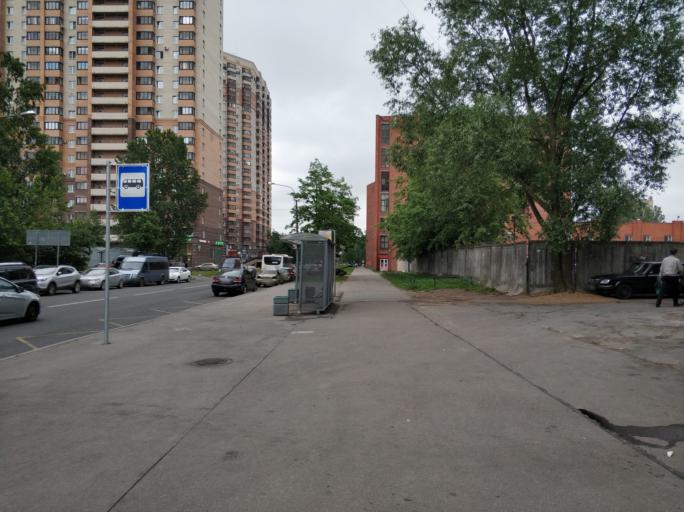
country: RU
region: St.-Petersburg
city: Grazhdanka
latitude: 60.0325
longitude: 30.4014
